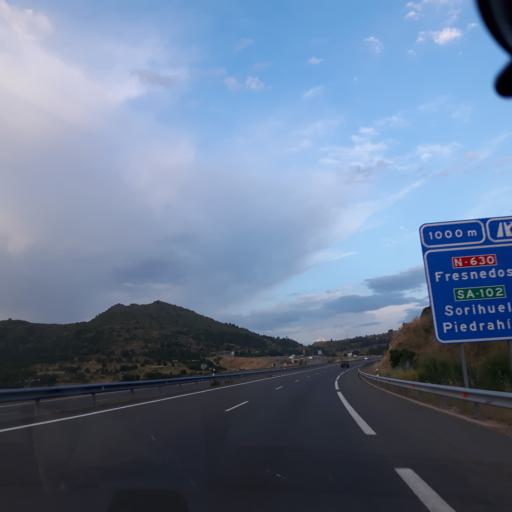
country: ES
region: Castille and Leon
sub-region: Provincia de Salamanca
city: Sorihuela
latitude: 40.4423
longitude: -5.6882
